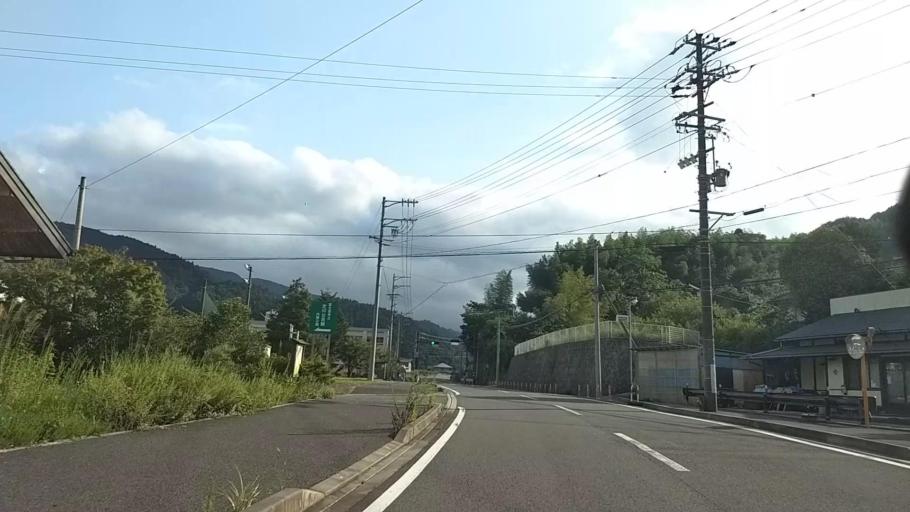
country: JP
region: Shizuoka
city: Fujinomiya
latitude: 35.1944
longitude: 138.5502
